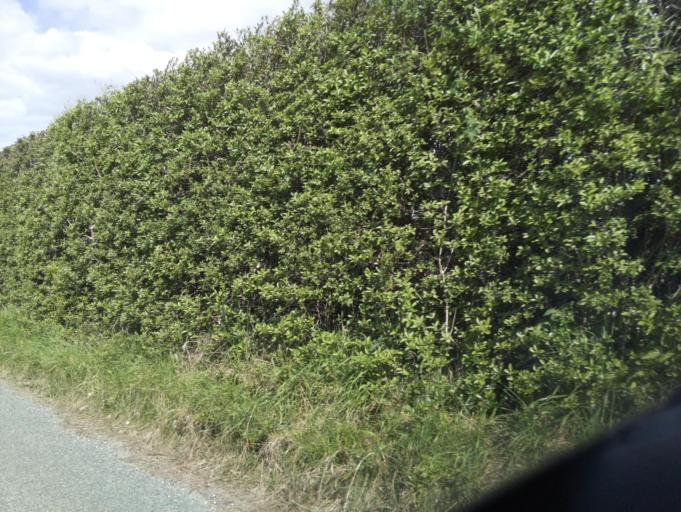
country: GB
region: England
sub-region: West Berkshire
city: Kintbury
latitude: 51.3714
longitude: -1.4831
